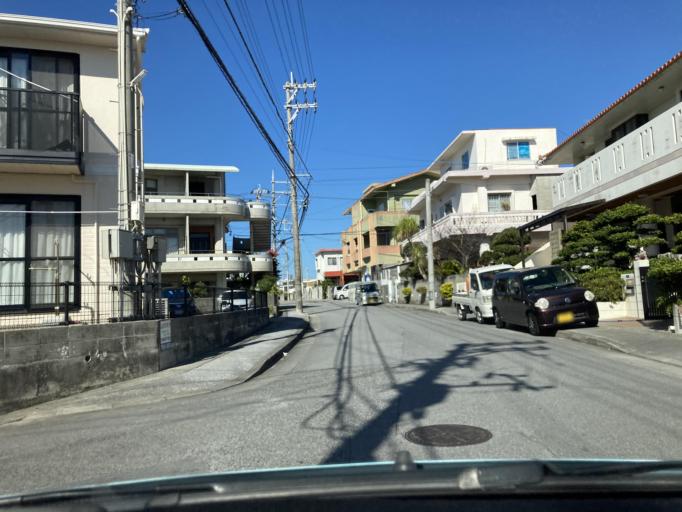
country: JP
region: Okinawa
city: Okinawa
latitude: 26.3476
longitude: 127.8269
